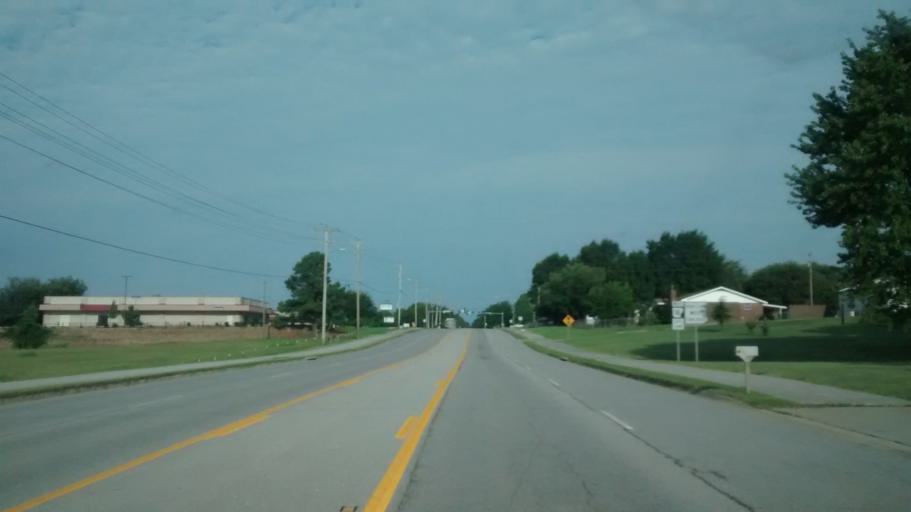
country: US
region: Arkansas
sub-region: Washington County
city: Farmington
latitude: 36.0793
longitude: -94.2493
